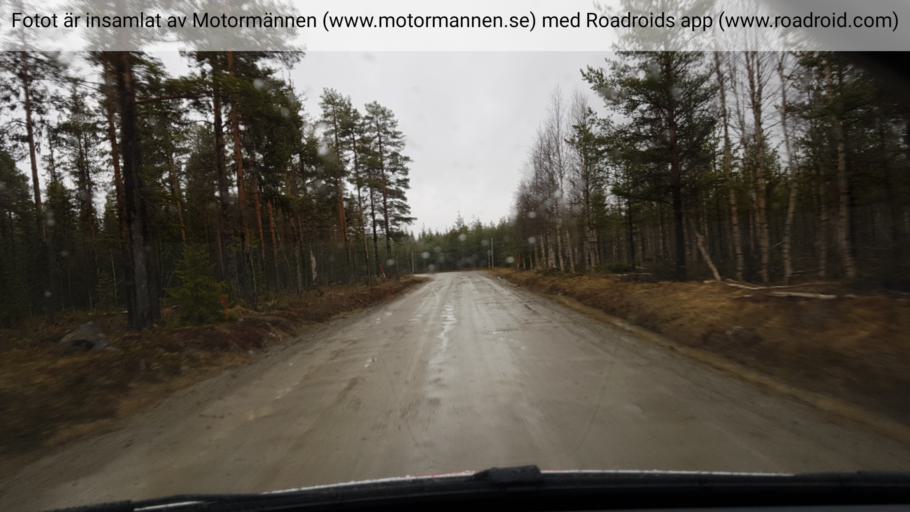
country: SE
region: Jaemtland
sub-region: Are Kommun
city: Jarpen
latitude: 62.4782
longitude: 13.5163
